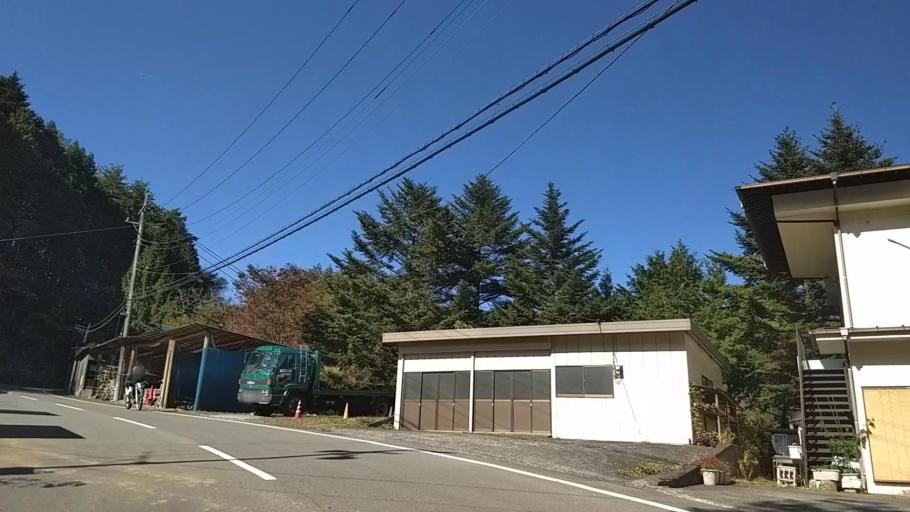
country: JP
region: Yamanashi
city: Otsuki
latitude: 35.7480
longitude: 138.9613
